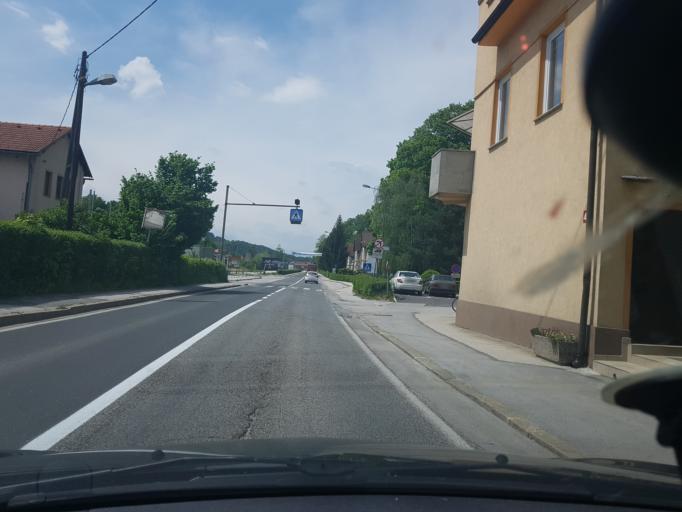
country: SI
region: Store
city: Store
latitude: 46.2216
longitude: 15.3225
